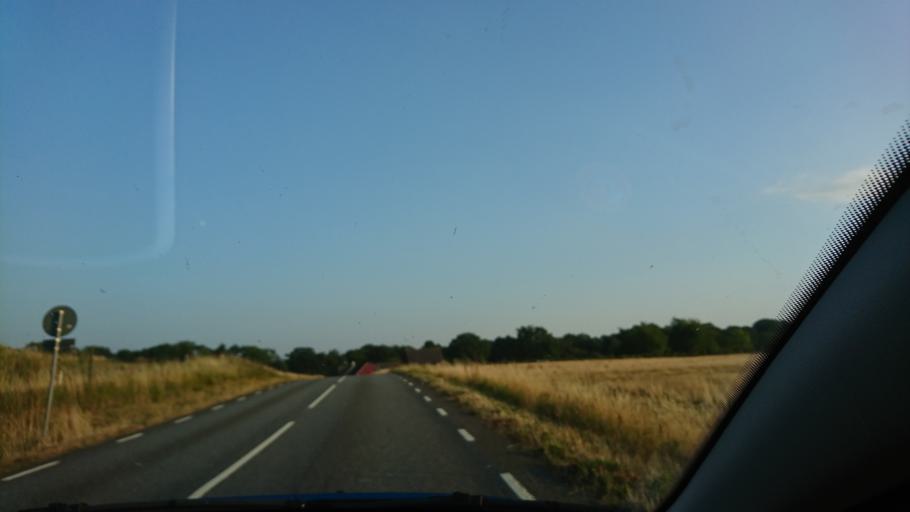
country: SE
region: Skane
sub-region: Simrishamns Kommun
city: Kivik
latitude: 55.7031
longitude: 14.1504
